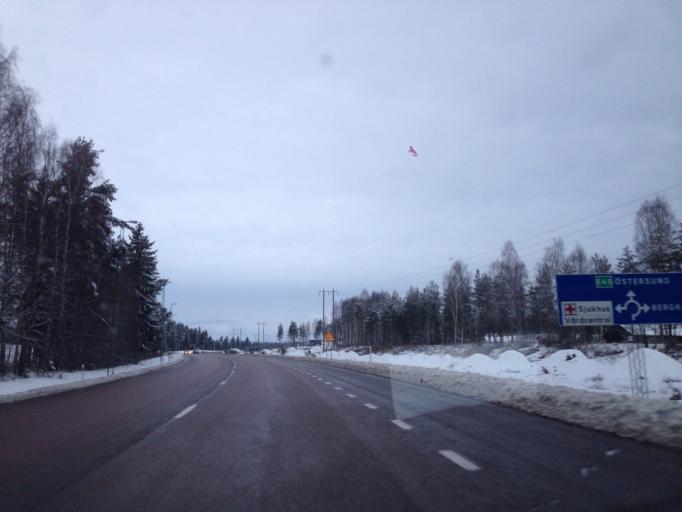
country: SE
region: Dalarna
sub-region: Mora Kommun
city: Mora
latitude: 61.0135
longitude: 14.5907
